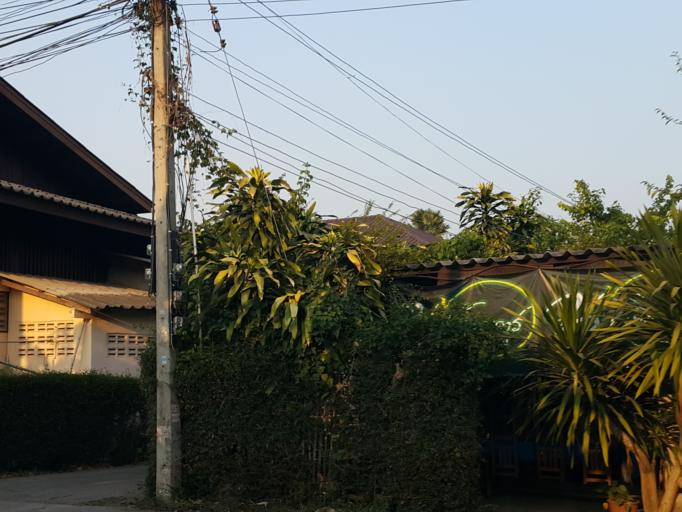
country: TH
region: Chiang Mai
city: San Sai
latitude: 18.8964
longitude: 98.9486
